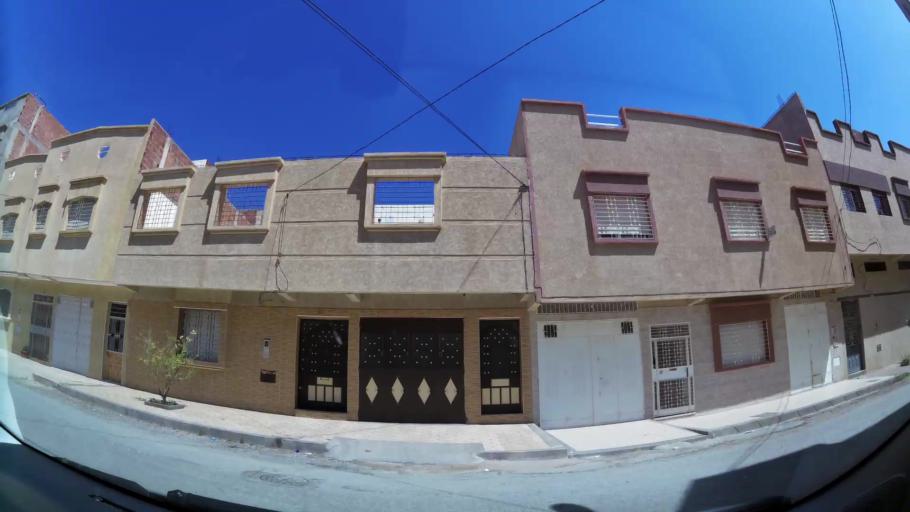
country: MA
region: Oriental
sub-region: Oujda-Angad
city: Oujda
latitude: 34.6772
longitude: -1.9422
